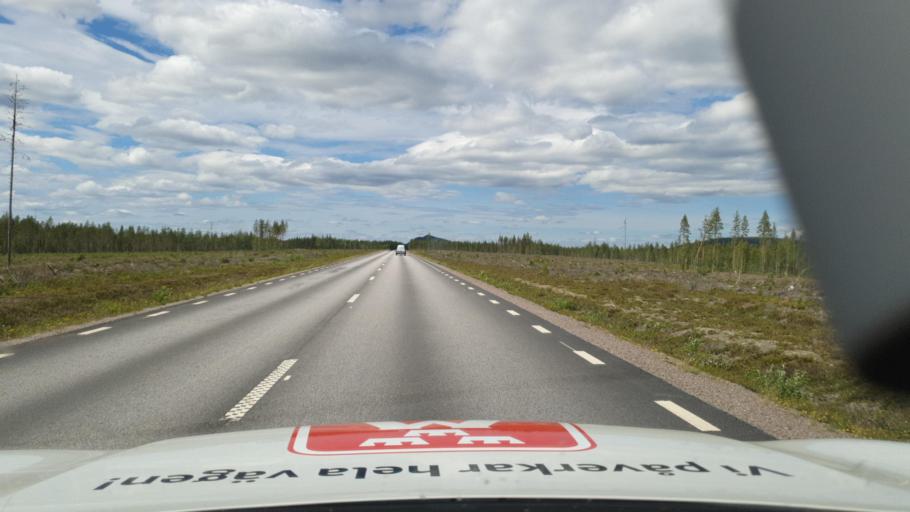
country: SE
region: Vaesterbotten
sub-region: Skelleftea Kommun
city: Langsele
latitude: 65.1234
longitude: 19.9425
